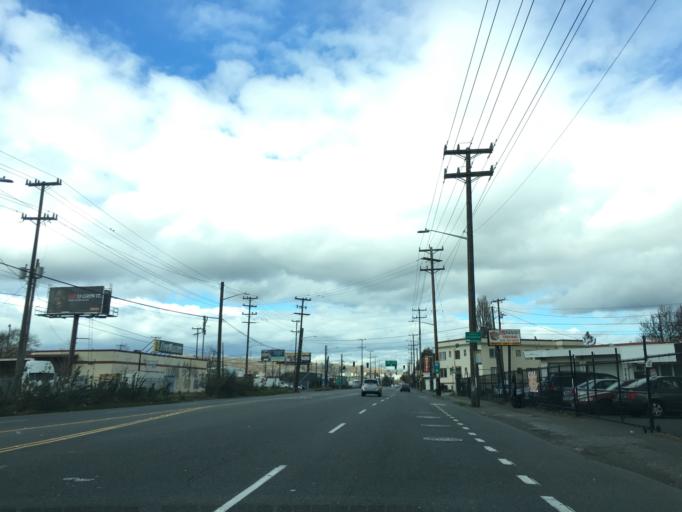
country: US
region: Washington
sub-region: King County
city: White Center
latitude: 47.5389
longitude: -122.3208
